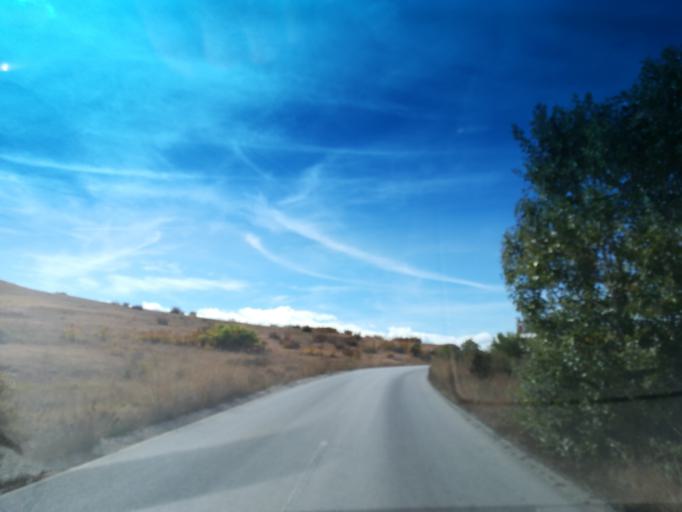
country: BG
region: Plovdiv
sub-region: Obshtina Krichim
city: Krichim
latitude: 42.0977
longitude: 24.4641
